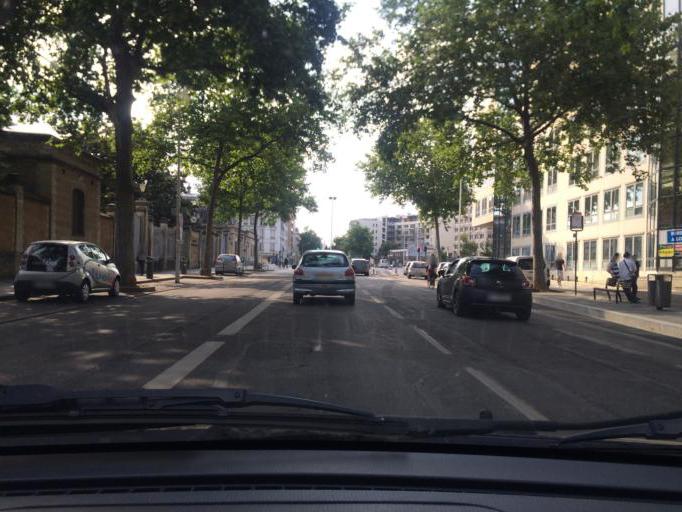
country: FR
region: Rhone-Alpes
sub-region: Departement du Rhone
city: Lyon
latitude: 45.7489
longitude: 4.8616
